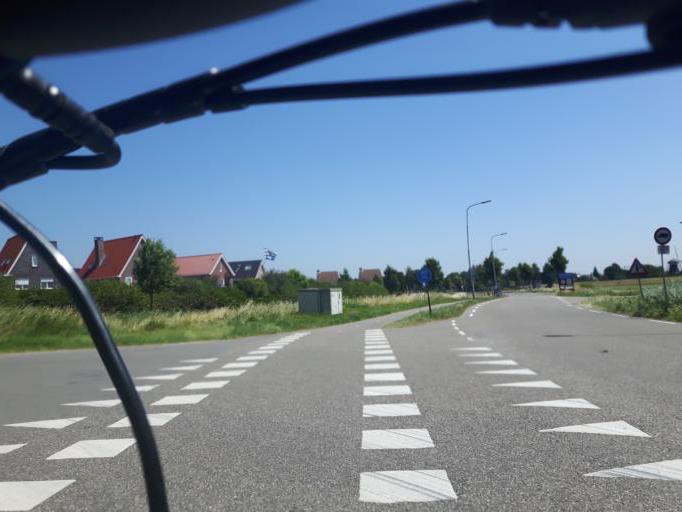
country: NL
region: Zeeland
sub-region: Gemeente Veere
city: Veere
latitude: 51.5040
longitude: 3.6643
